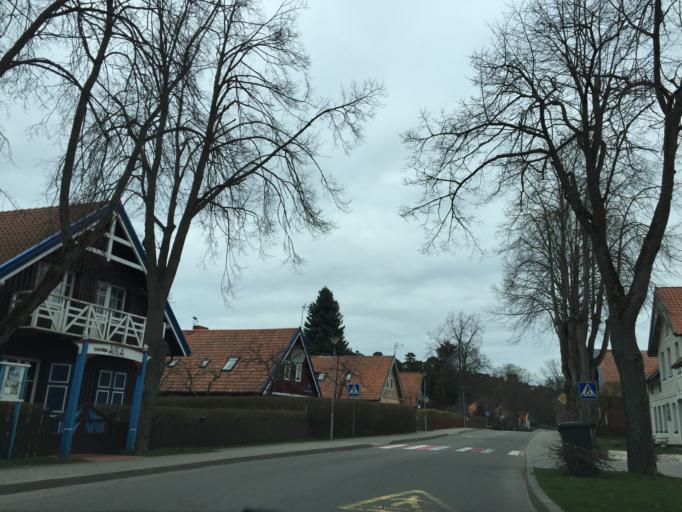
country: LT
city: Nida
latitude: 55.3068
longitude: 21.0057
